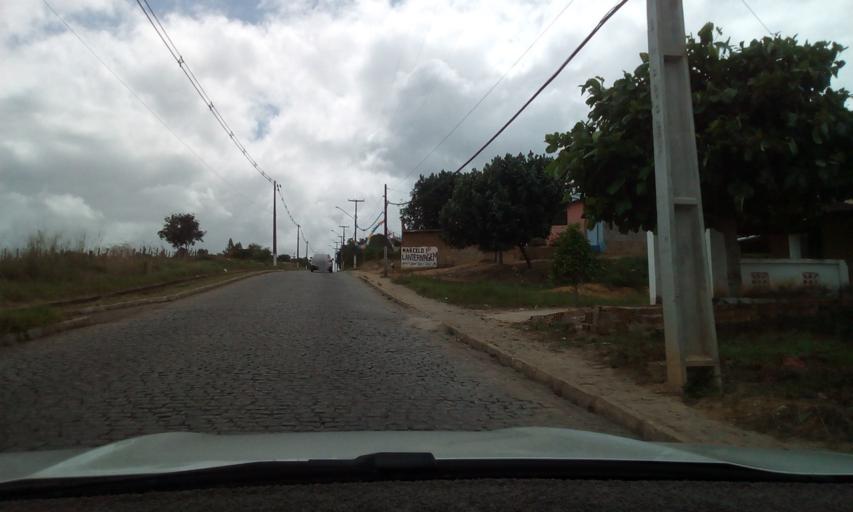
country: BR
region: Paraiba
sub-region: Rio Tinto
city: Rio Tinto
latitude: -6.7961
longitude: -35.0698
